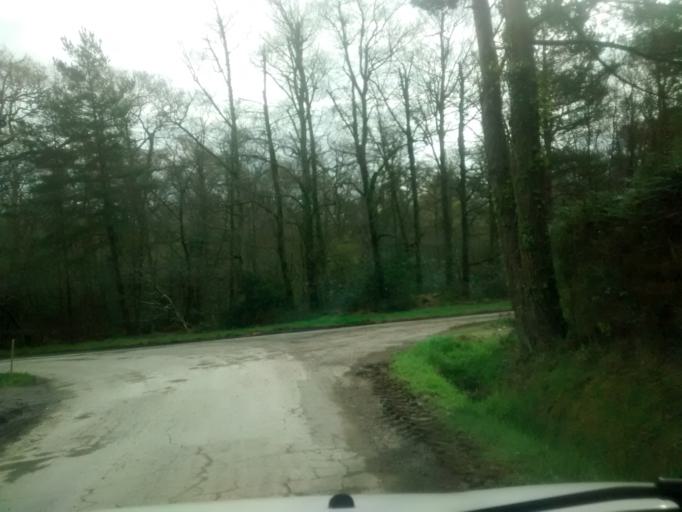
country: FR
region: Brittany
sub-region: Departement d'Ille-et-Vilaine
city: Chasne-sur-Illet
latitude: 48.2319
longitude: -1.5394
